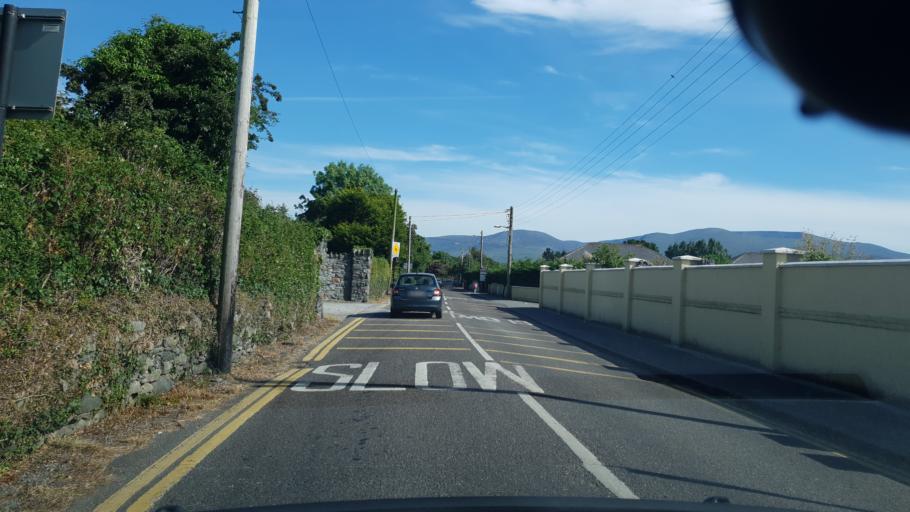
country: IE
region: Munster
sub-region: Ciarrai
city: Cill Airne
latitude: 52.0576
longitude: -9.4940
